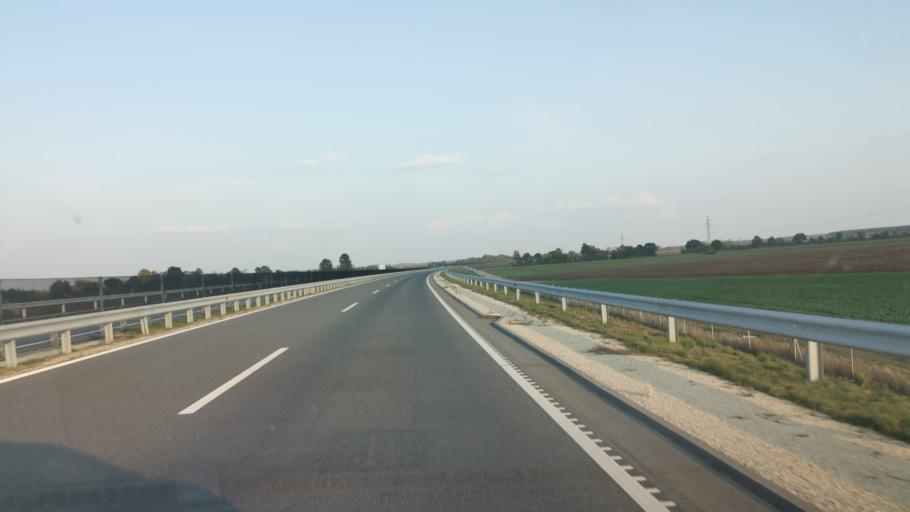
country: HU
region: Gyor-Moson-Sopron
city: Mihalyi
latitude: 47.5656
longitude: 17.1006
